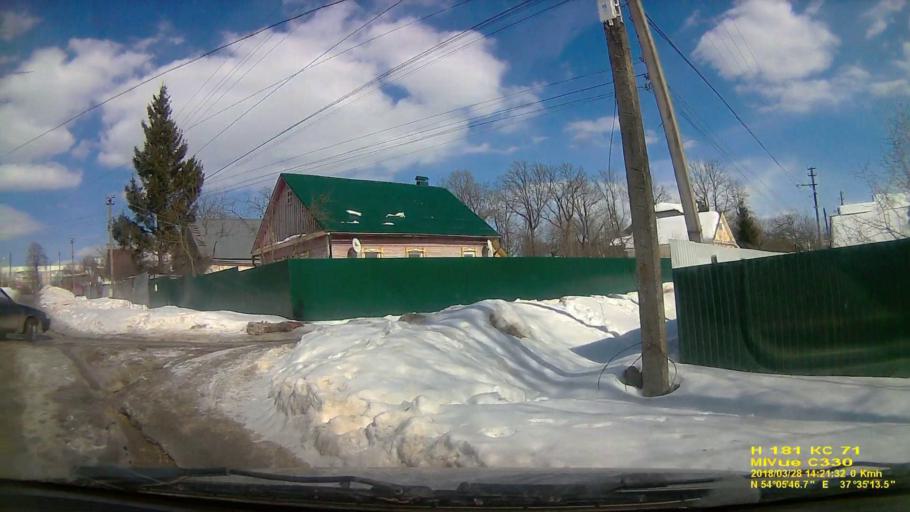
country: RU
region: Tula
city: Skuratovskiy
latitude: 54.0962
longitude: 37.5870
